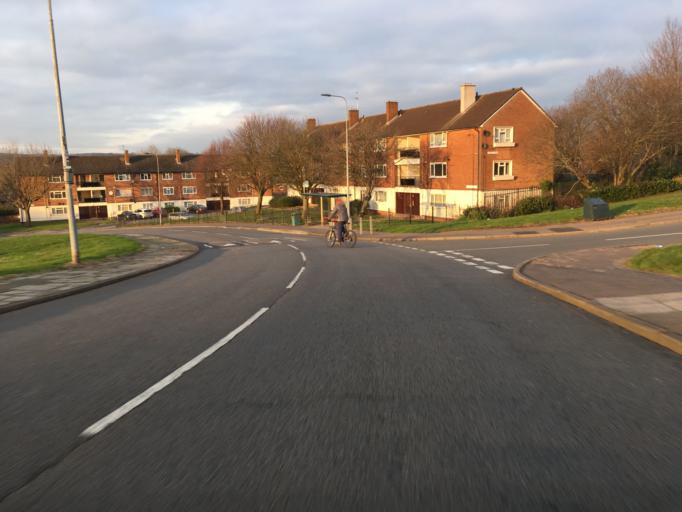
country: GB
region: Wales
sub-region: Newport
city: Marshfield
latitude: 51.5283
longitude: -3.1168
